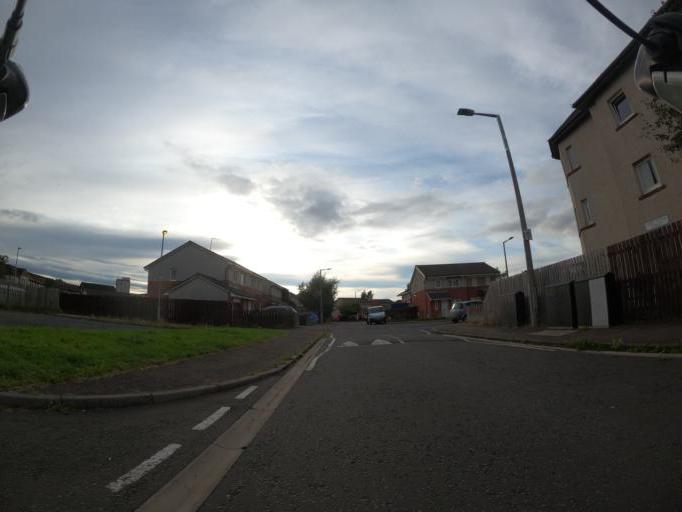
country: GB
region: Scotland
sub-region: Edinburgh
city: Edinburgh
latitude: 55.9735
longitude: -3.2452
